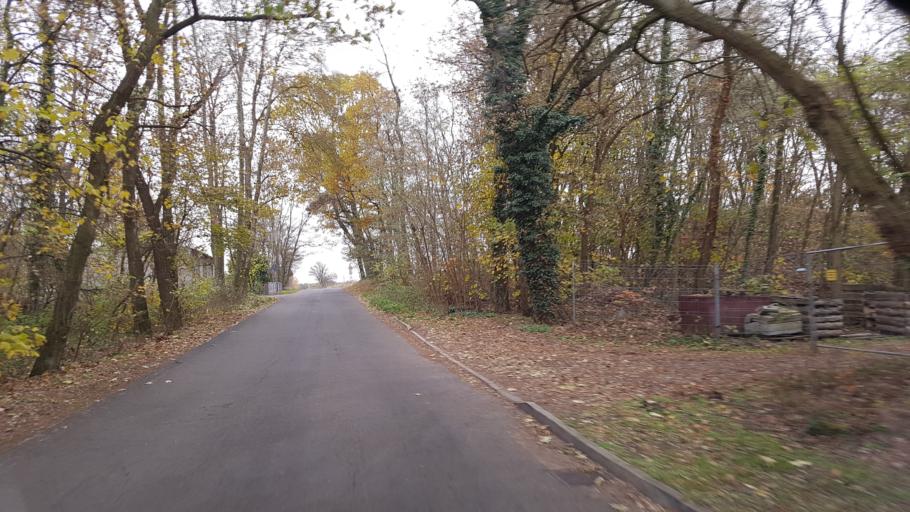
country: DE
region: Brandenburg
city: Crinitz
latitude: 51.7356
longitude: 13.7612
